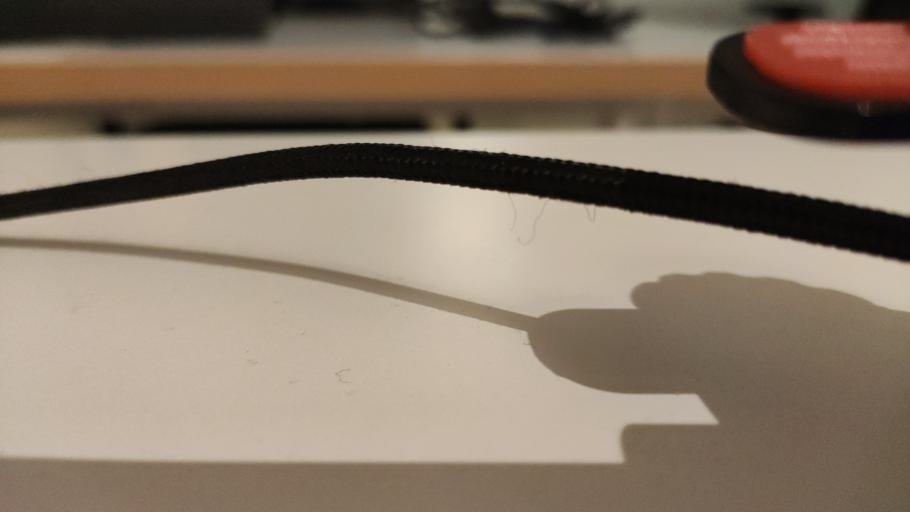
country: RU
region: Moskovskaya
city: Budenovetc
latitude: 56.3862
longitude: 37.6206
